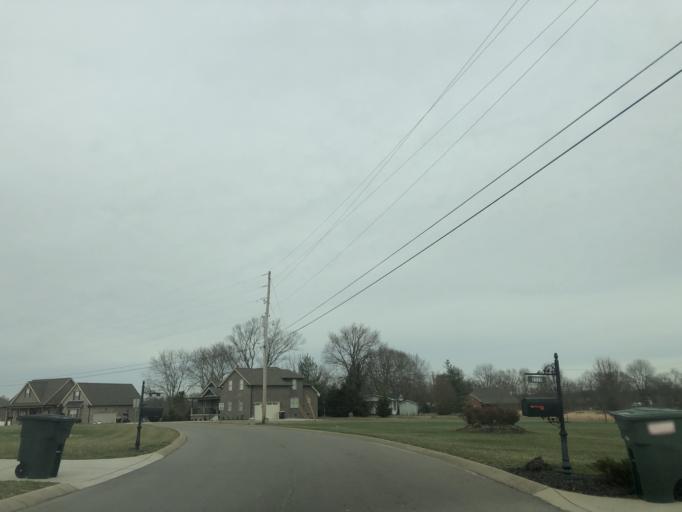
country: US
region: Tennessee
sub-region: Robertson County
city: Greenbrier
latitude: 36.4008
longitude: -86.8157
